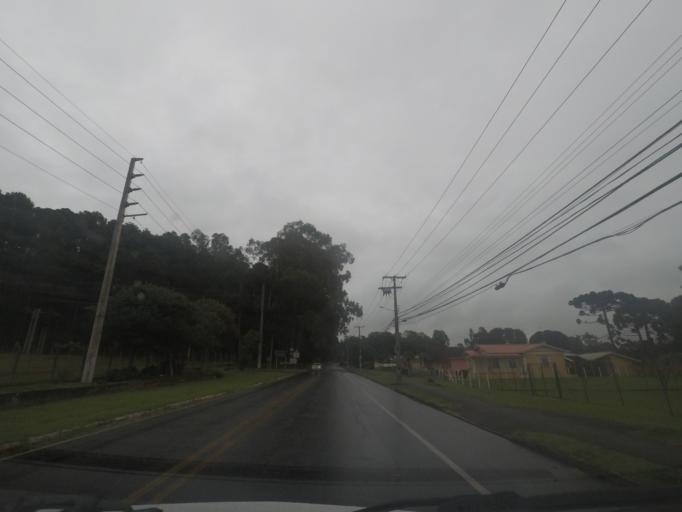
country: BR
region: Parana
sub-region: Quatro Barras
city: Quatro Barras
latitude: -25.3818
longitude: -49.1290
